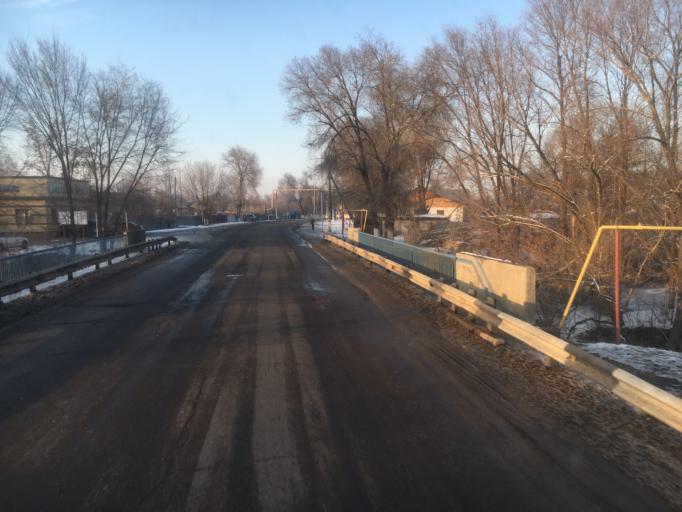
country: KZ
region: Almaty Oblysy
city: Burunday
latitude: 43.3662
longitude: 76.6415
